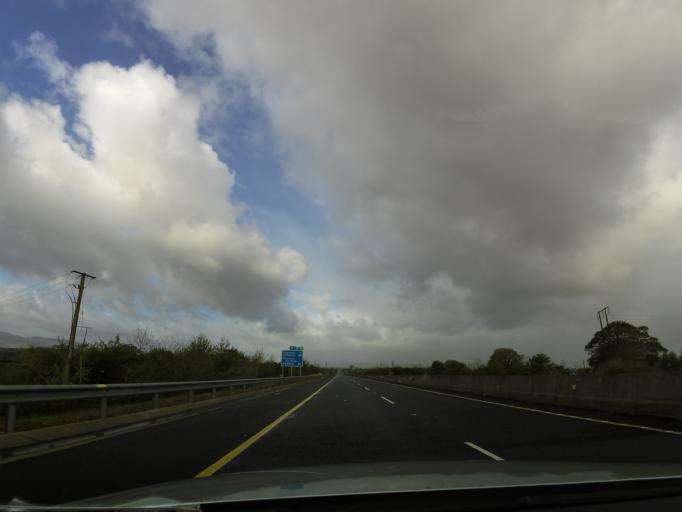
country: IE
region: Munster
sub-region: North Tipperary
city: Nenagh
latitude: 52.8489
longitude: -8.1650
